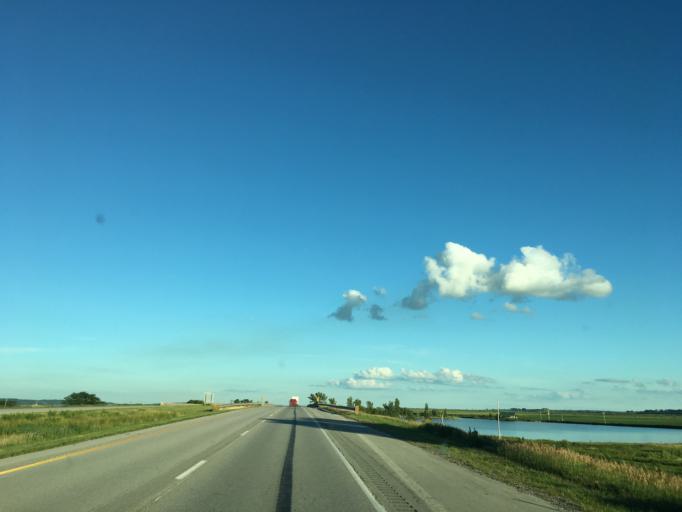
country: US
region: Nebraska
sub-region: Otoe County
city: Nebraska City
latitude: 40.6708
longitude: -95.7673
